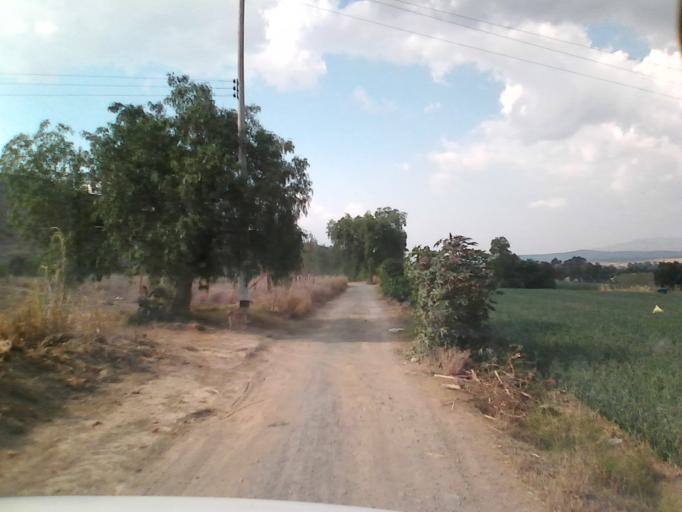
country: CO
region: Boyaca
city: Sachica
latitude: 5.5878
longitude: -73.5467
